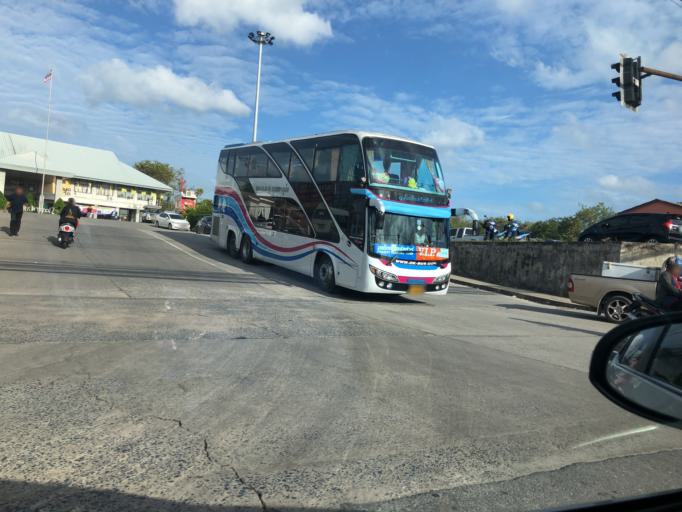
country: TH
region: Phuket
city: Ban Ratsada
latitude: 7.9180
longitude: 98.3949
